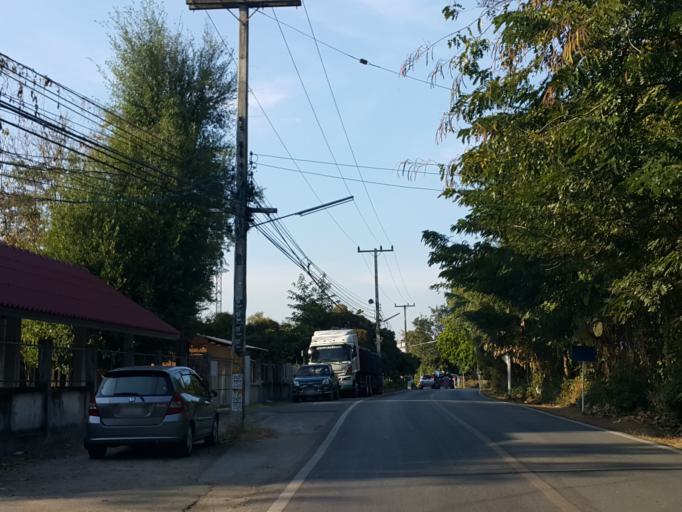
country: TH
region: Chiang Mai
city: San Sai
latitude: 18.7920
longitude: 99.0608
